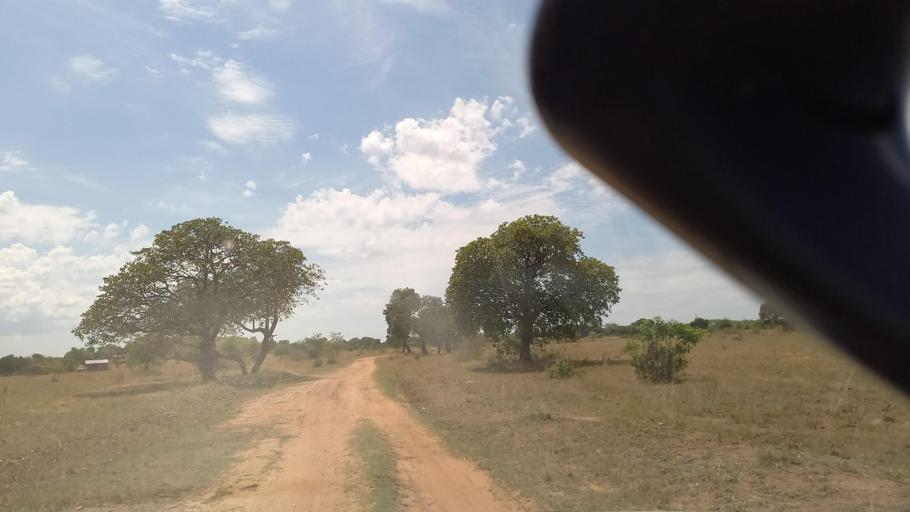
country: ZM
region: Southern
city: Mazabuka
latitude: -16.1463
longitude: 27.7743
